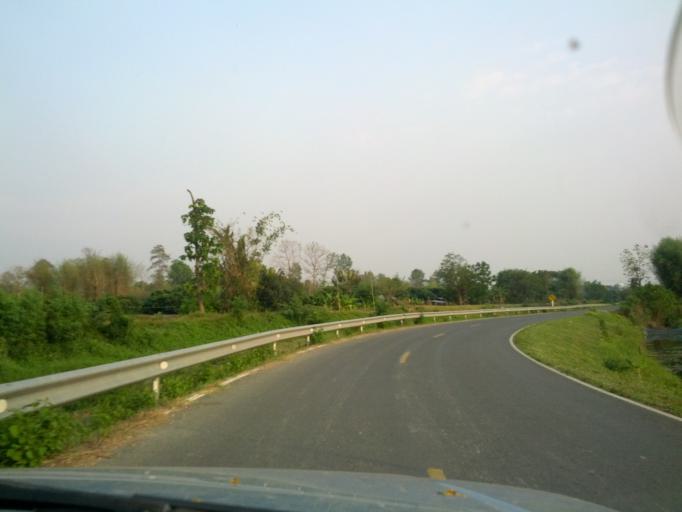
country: TH
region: Chiang Mai
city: San Sai
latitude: 18.9415
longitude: 98.9949
